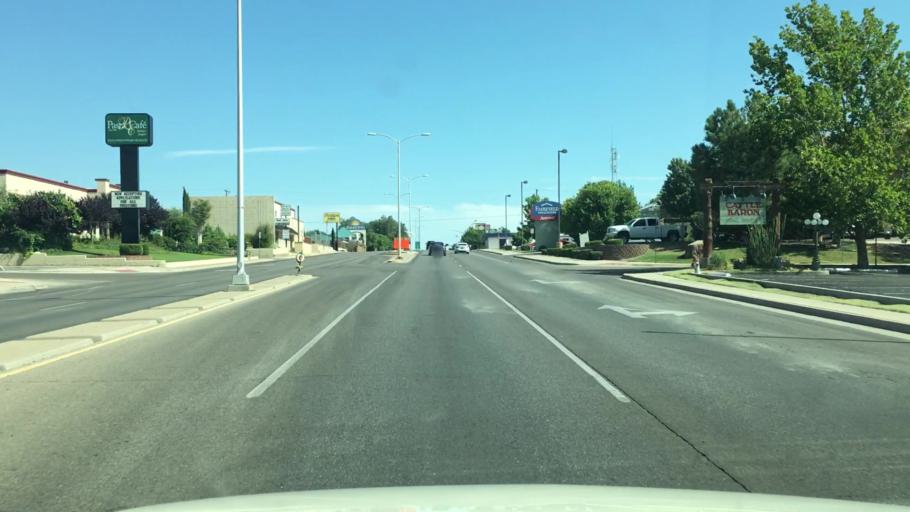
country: US
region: New Mexico
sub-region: Chaves County
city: Roswell
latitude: 33.4053
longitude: -104.5228
